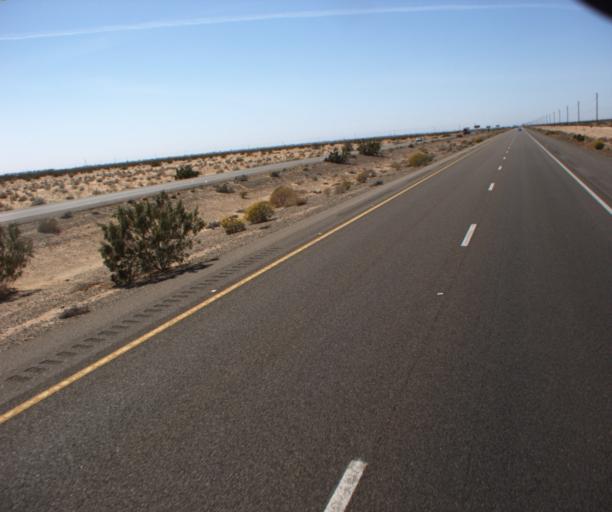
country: MX
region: Sonora
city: San Luis Rio Colorado
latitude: 32.4947
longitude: -114.6728
